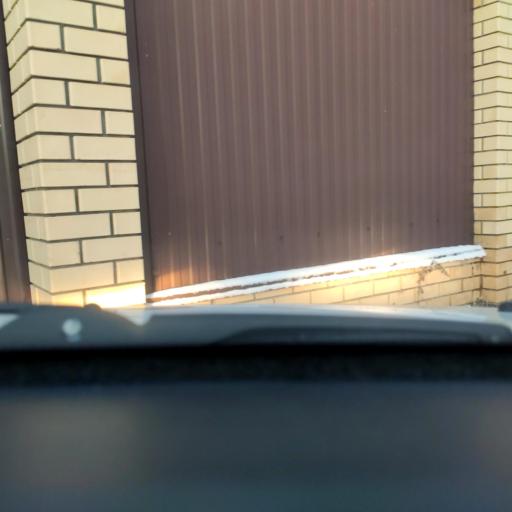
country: RU
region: Perm
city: Perm
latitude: 58.0355
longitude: 56.2523
